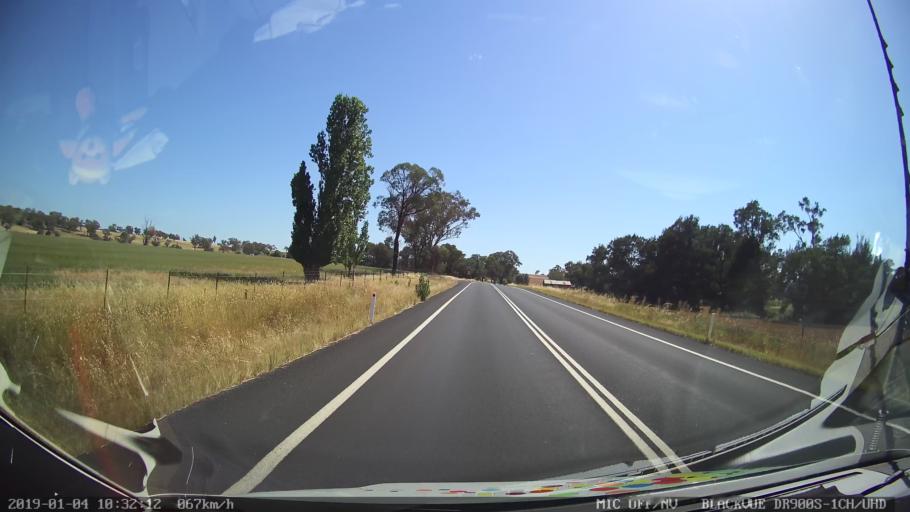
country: AU
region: New South Wales
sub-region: Cabonne
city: Canowindra
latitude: -33.3283
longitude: 148.6371
